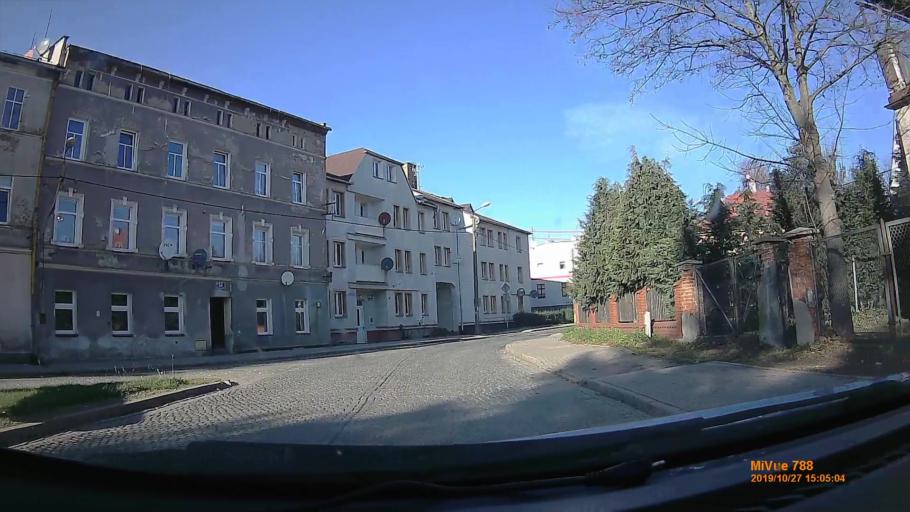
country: PL
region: Lower Silesian Voivodeship
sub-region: Powiat klodzki
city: Miedzylesie
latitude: 50.1444
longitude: 16.6636
